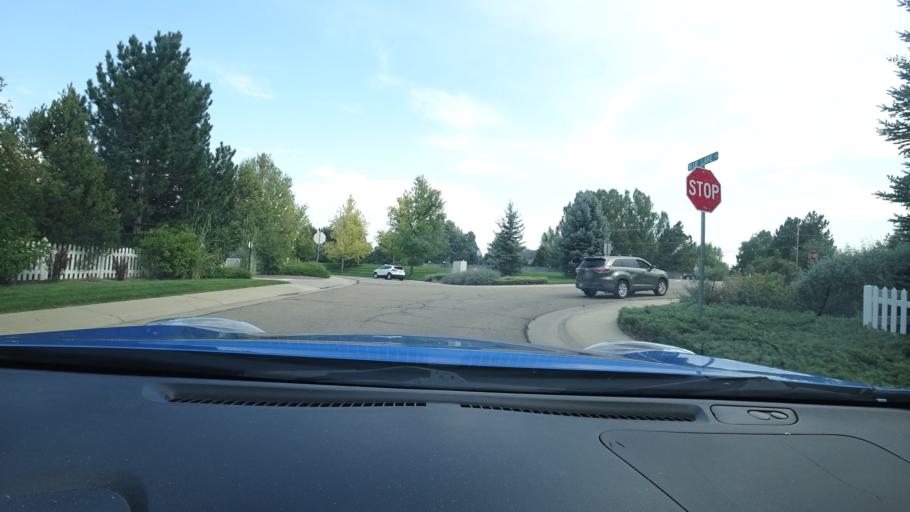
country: US
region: Colorado
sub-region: Boulder County
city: Louisville
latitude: 40.0006
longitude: -105.1380
